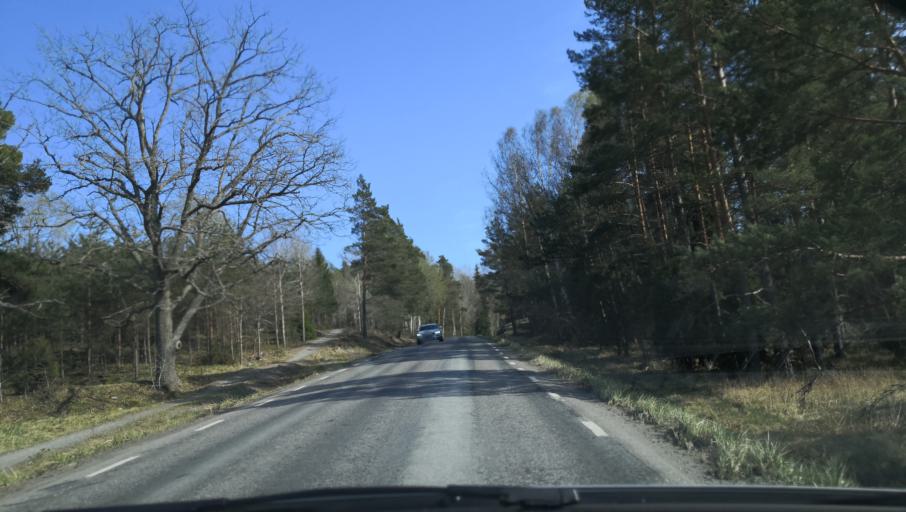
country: SE
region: Stockholm
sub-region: Varmdo Kommun
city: Hemmesta
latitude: 59.3245
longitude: 18.5475
